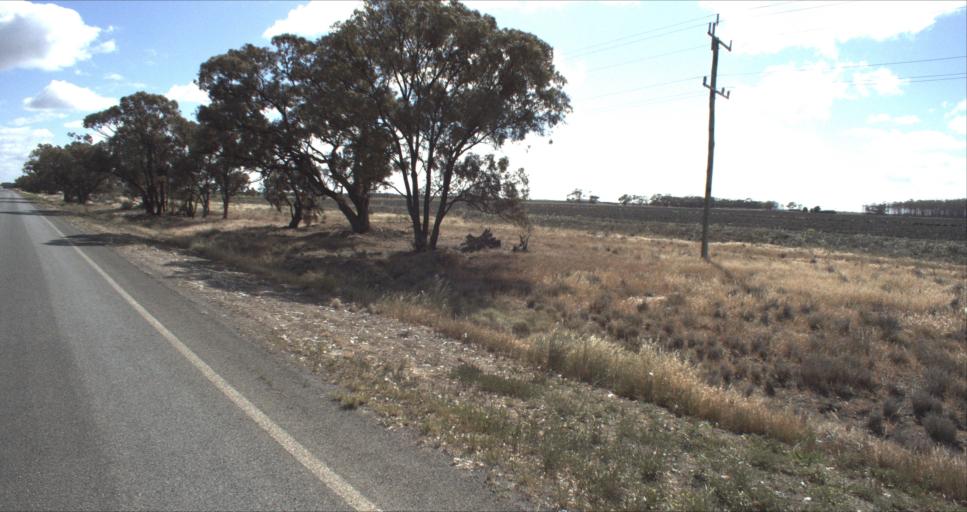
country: AU
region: New South Wales
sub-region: Murrumbidgee Shire
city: Darlington Point
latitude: -34.5602
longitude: 146.1692
